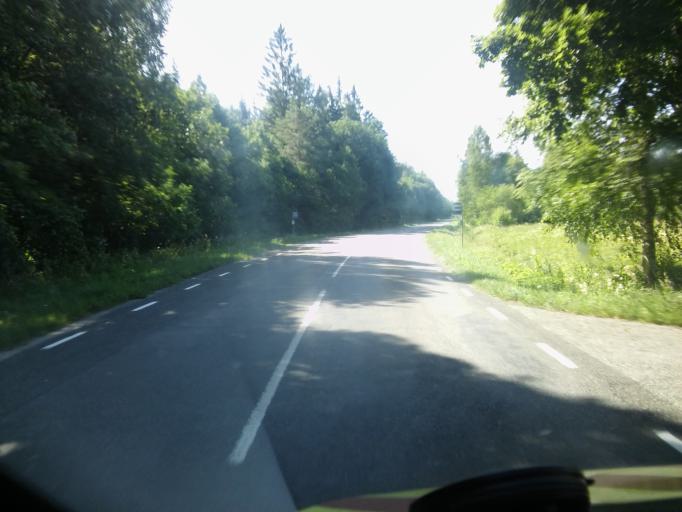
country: EE
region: Paernumaa
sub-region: Paikuse vald
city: Paikuse
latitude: 58.2941
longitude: 24.6921
